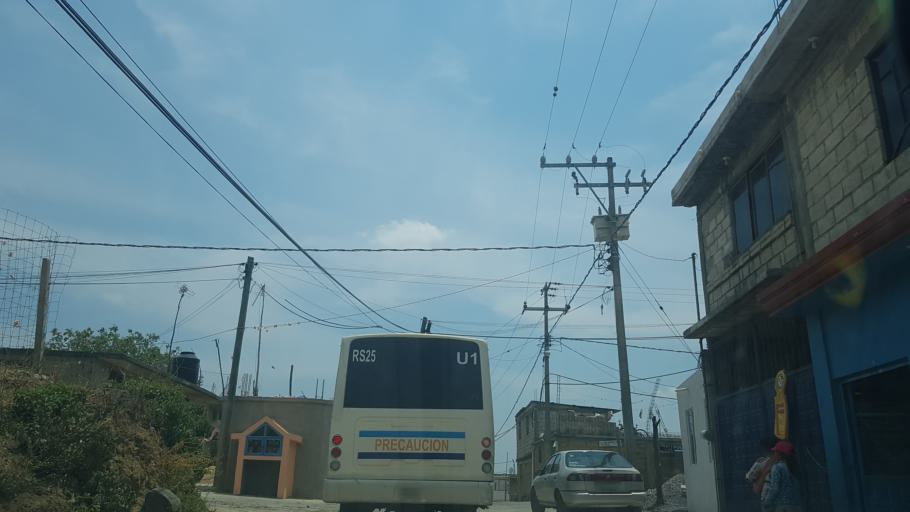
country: MX
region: Puebla
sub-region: Tochimilco
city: Santa Cruz Cuautomatitla
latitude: 18.8784
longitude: -98.6196
